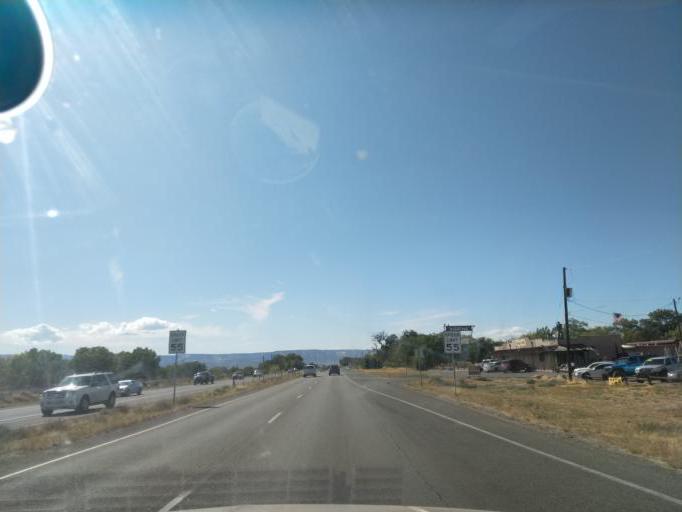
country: US
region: Colorado
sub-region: Mesa County
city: Fruitvale
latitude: 39.0827
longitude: -108.4745
